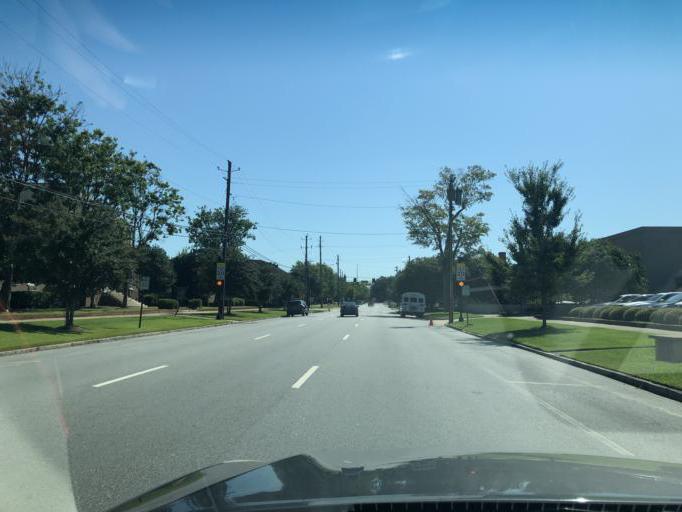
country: US
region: Georgia
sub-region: Muscogee County
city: Columbus
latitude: 32.4667
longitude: -84.9901
